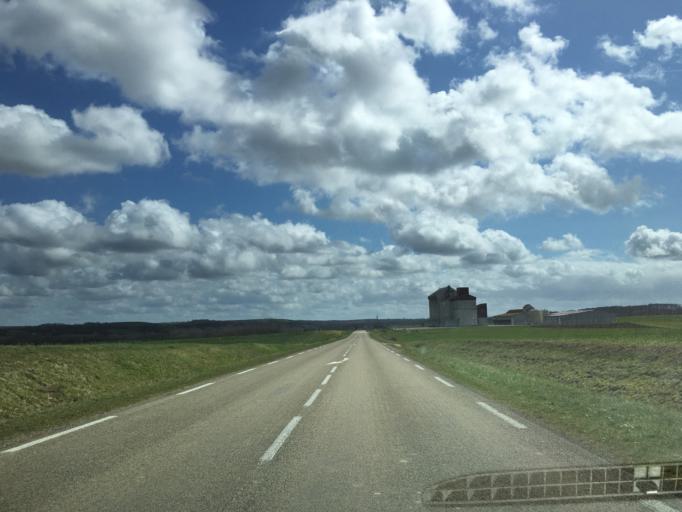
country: FR
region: Bourgogne
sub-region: Departement de l'Yonne
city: Aillant-sur-Tholon
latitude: 47.8526
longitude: 3.3771
